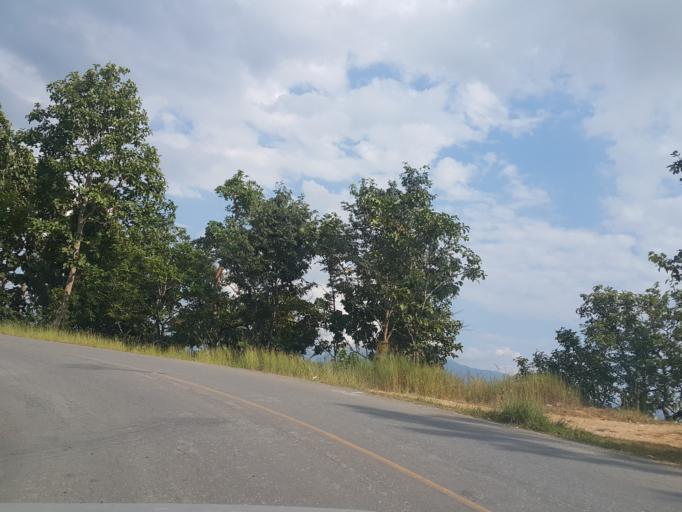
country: TH
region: Chiang Mai
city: Mae Chaem
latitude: 18.5306
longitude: 98.3680
